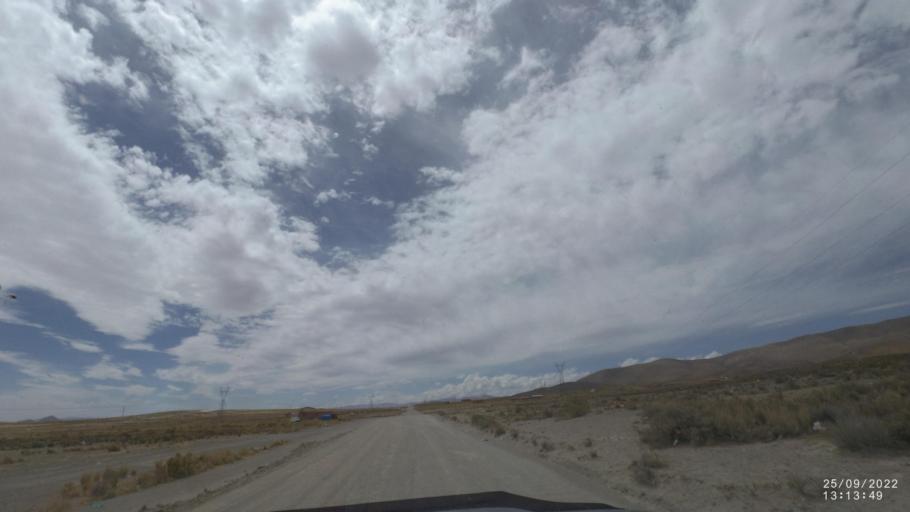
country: BO
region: Oruro
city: Oruro
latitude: -17.9448
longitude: -67.0397
